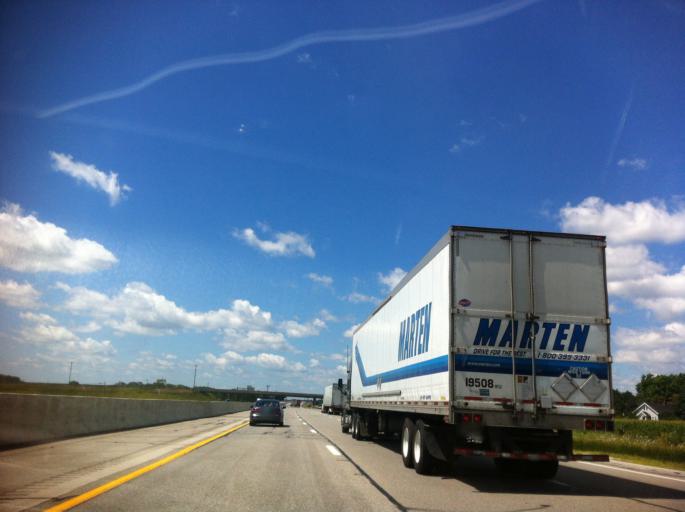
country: US
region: Ohio
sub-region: Wood County
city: Millbury
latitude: 41.5282
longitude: -83.4690
